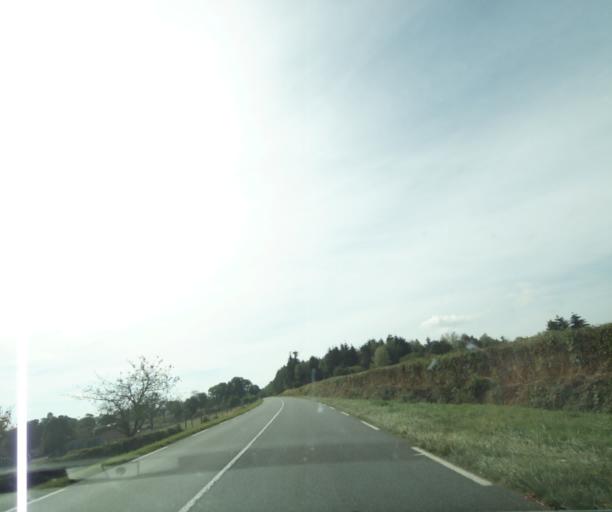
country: FR
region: Auvergne
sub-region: Departement de l'Allier
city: Le Donjon
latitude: 46.3264
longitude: 3.7665
